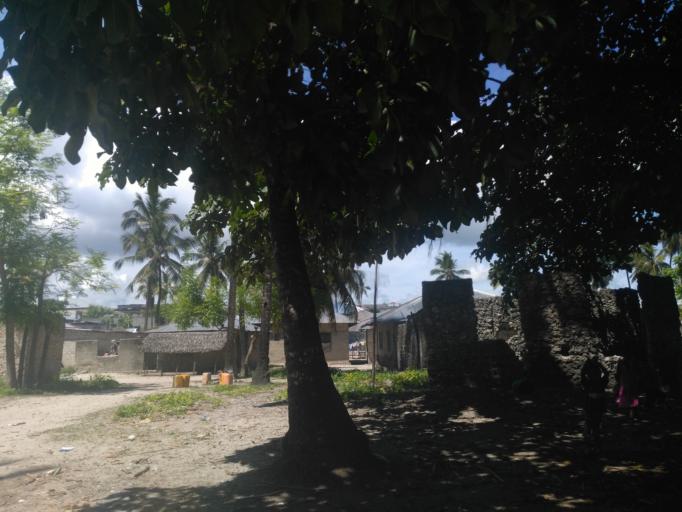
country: TZ
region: Zanzibar North
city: Gamba
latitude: -5.9238
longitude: 39.3576
